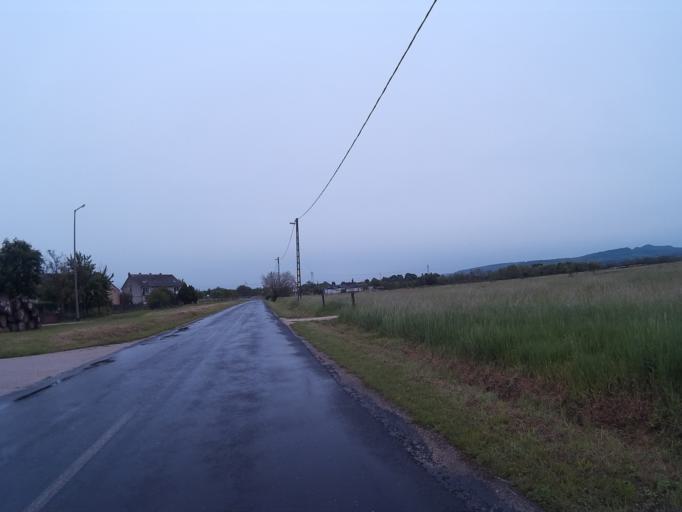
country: HU
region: Veszprem
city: Sumeg
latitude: 46.9690
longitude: 17.2890
